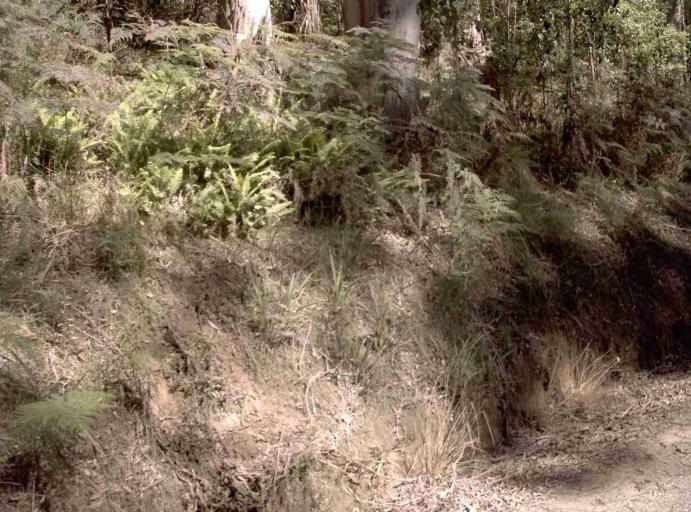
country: AU
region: New South Wales
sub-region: Bombala
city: Bombala
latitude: -37.2241
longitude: 148.7479
